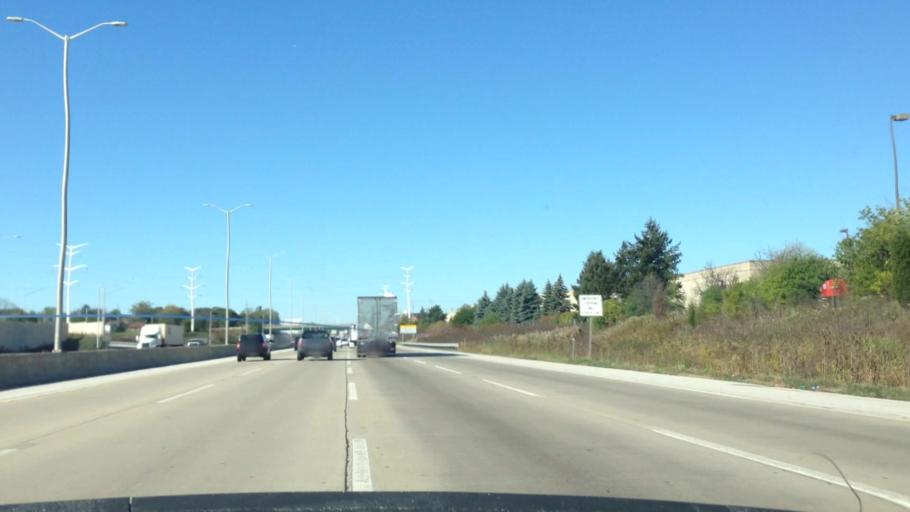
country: US
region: Illinois
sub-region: DuPage County
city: Oakbrook Terrace
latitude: 41.8446
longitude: -87.9661
